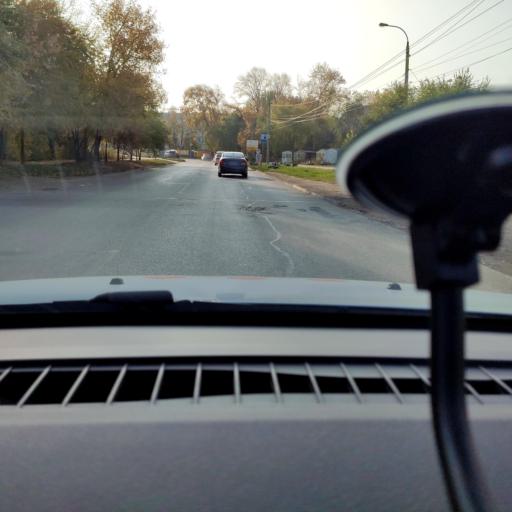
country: RU
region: Samara
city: Samara
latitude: 53.1882
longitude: 50.1727
